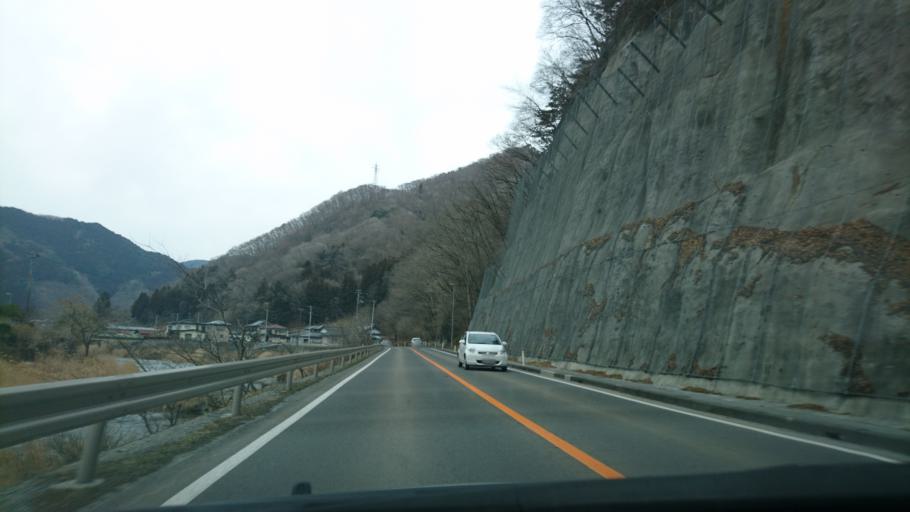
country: JP
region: Iwate
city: Tono
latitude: 39.1475
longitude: 141.5465
